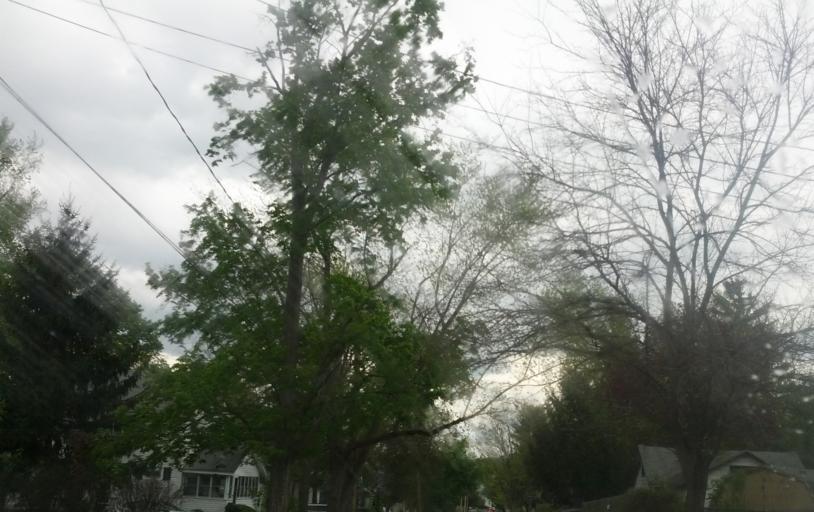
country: US
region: New York
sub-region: Onondaga County
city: Nedrow
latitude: 43.0040
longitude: -76.1585
